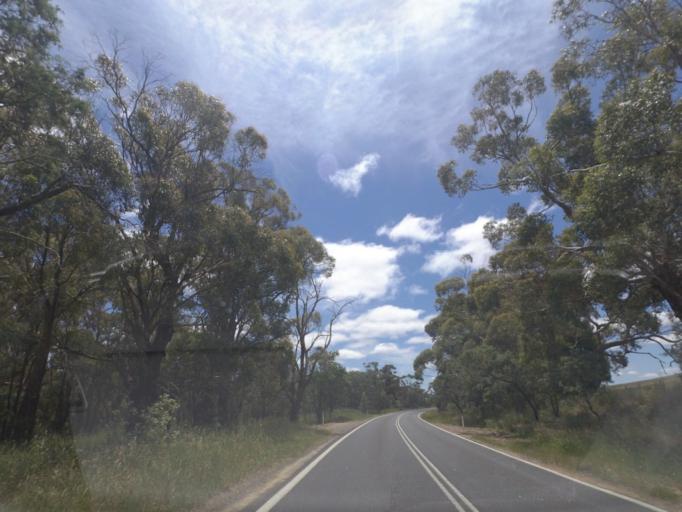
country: AU
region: Victoria
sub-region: Mount Alexander
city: Castlemaine
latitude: -37.3232
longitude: 144.1627
